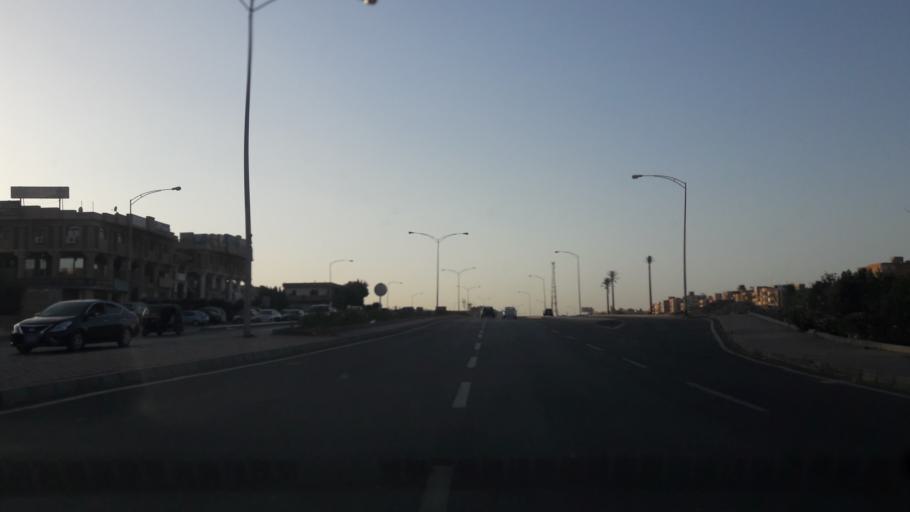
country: EG
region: Al Jizah
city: Madinat Sittah Uktubar
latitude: 29.9531
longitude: 30.9357
